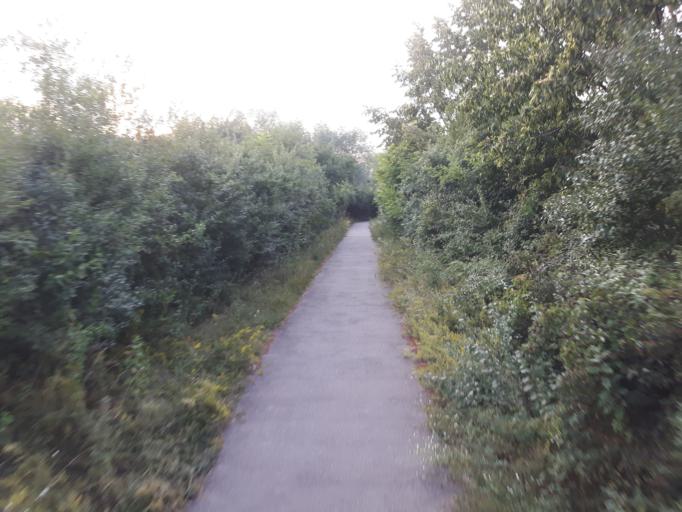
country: DE
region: Berlin
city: Staaken
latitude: 52.5480
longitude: 13.1476
